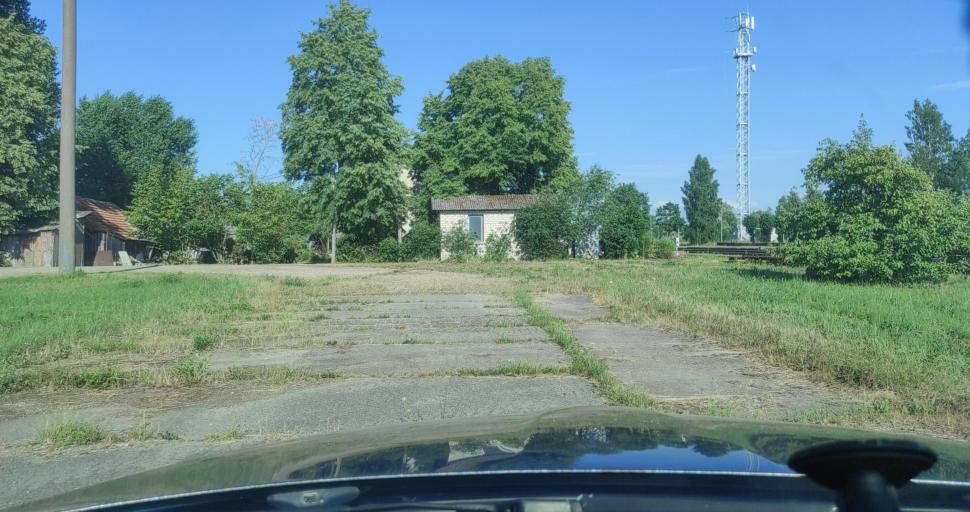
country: LV
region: Skrunda
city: Skrunda
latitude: 56.6809
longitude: 22.0120
